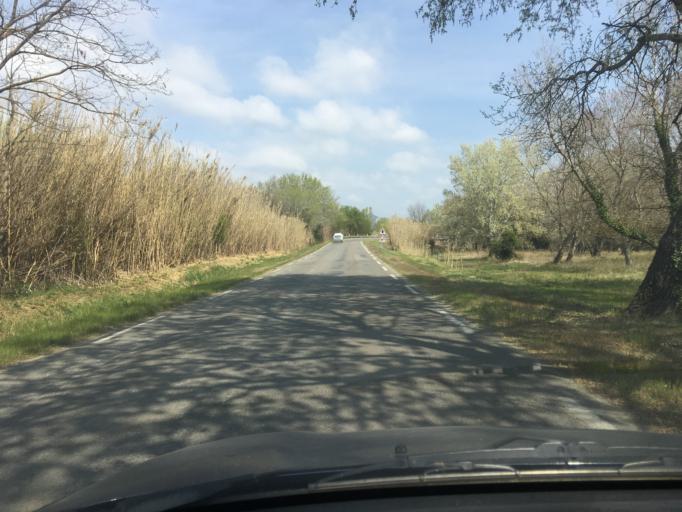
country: FR
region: Provence-Alpes-Cote d'Azur
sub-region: Departement du Vaucluse
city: Loriol-du-Comtat
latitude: 44.0989
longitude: 4.9981
